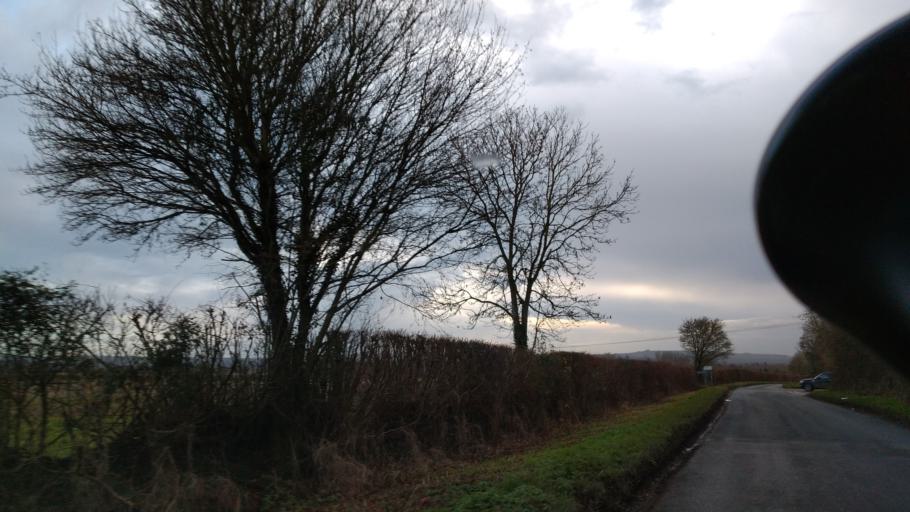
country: GB
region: England
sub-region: Borough of Swindon
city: Highworth
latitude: 51.6052
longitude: -1.7282
